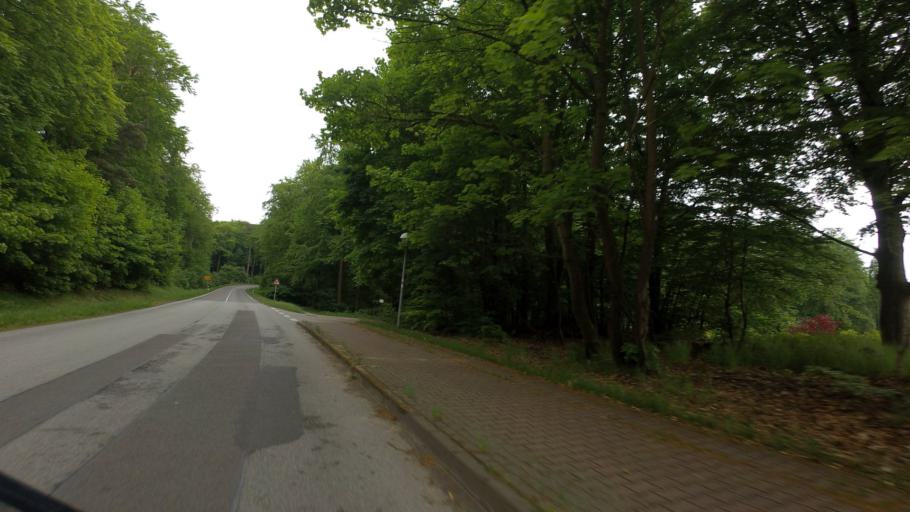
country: DE
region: Brandenburg
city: Lychen
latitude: 53.1974
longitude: 13.3251
